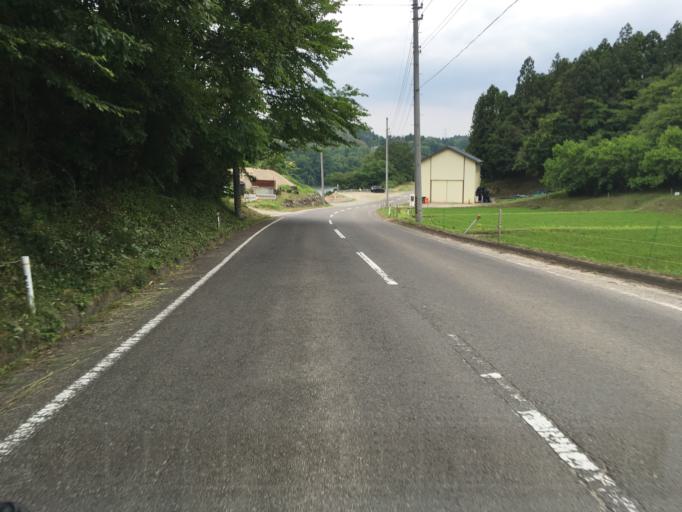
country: JP
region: Fukushima
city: Nihommatsu
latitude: 37.6234
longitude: 140.5241
